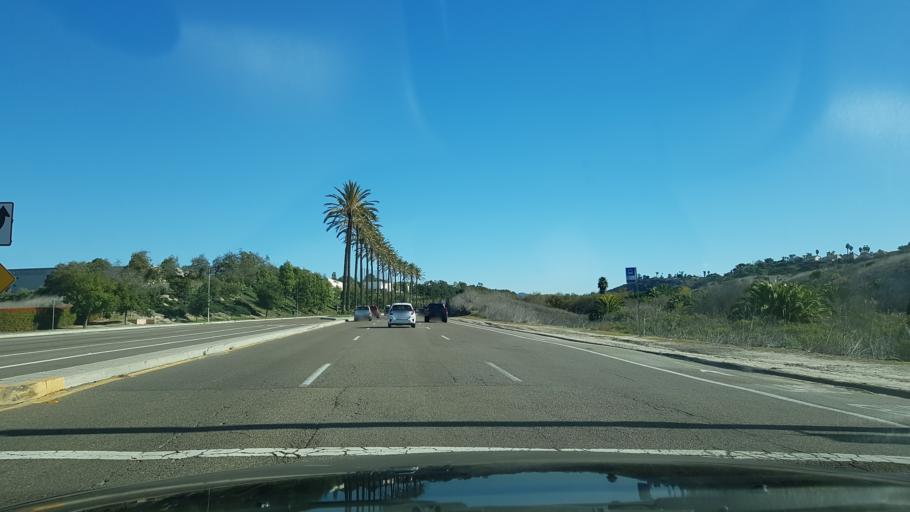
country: US
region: California
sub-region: San Diego County
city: Carlsbad
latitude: 33.2031
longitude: -117.3109
